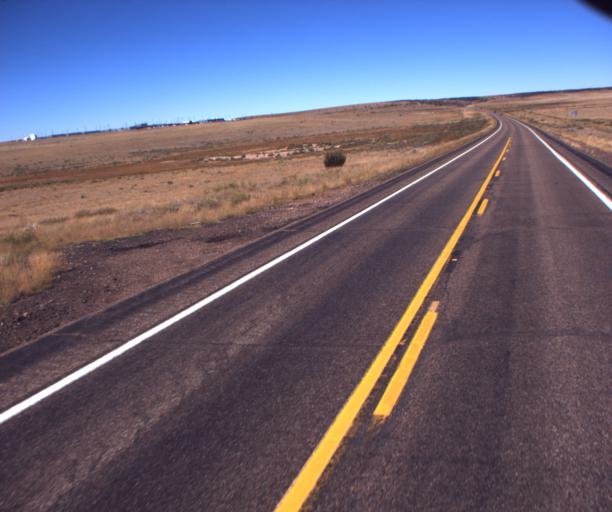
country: US
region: Arizona
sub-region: Apache County
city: Saint Johns
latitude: 34.3141
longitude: -109.3807
